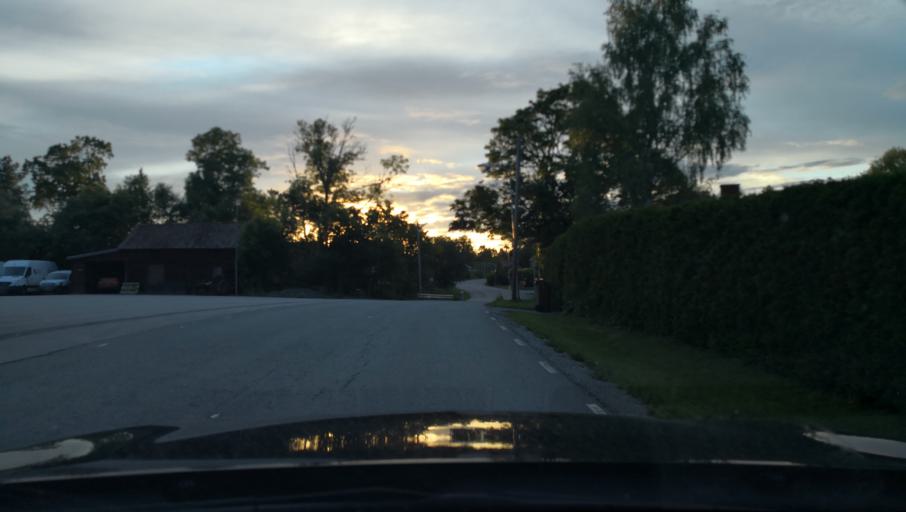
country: SE
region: Uppsala
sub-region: Enkopings Kommun
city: Grillby
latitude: 59.6574
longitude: 17.2465
